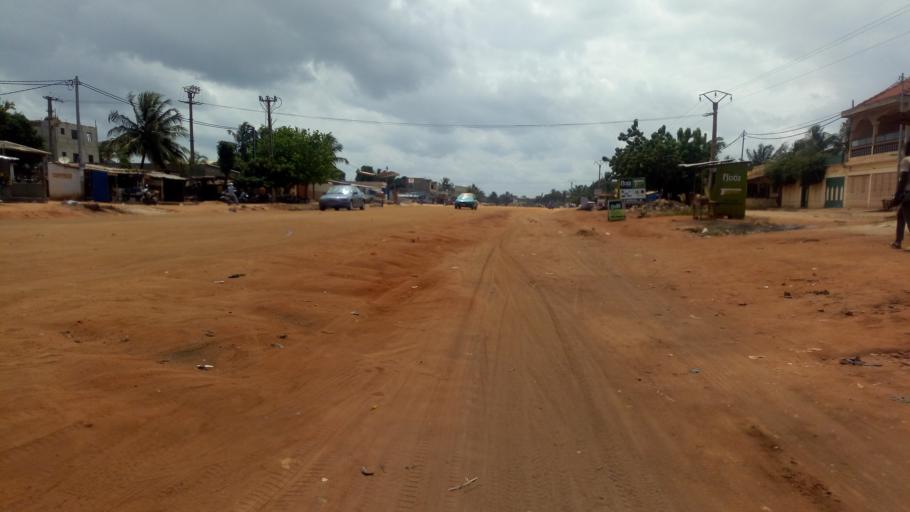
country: TG
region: Maritime
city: Lome
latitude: 6.2162
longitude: 1.1848
